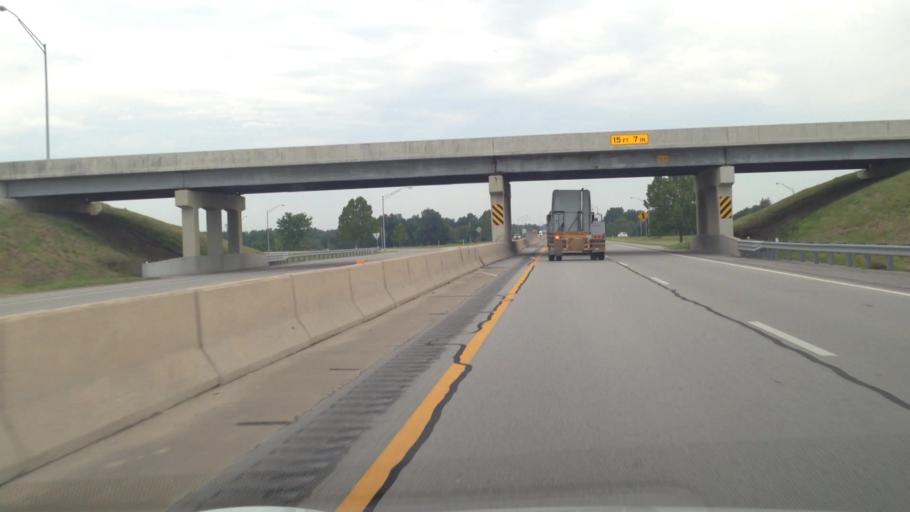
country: US
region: Oklahoma
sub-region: Ottawa County
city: Miami
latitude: 36.8661
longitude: -94.8497
